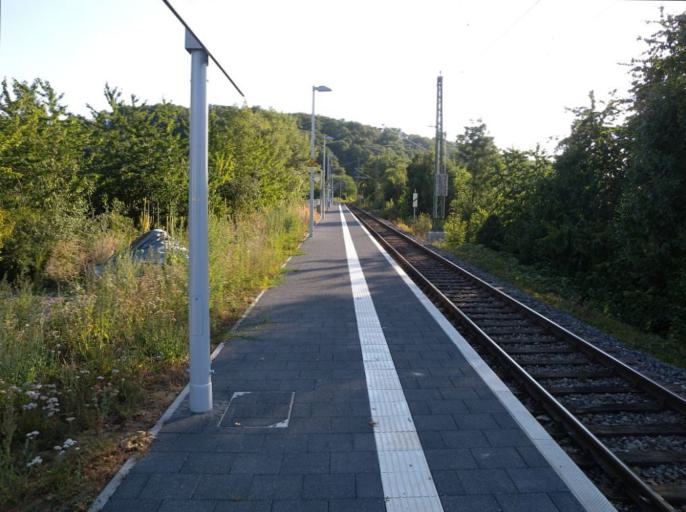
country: DE
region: Baden-Wuerttemberg
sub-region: Regierungsbezirk Stuttgart
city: Untereisesheim
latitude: 49.2302
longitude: 9.1882
